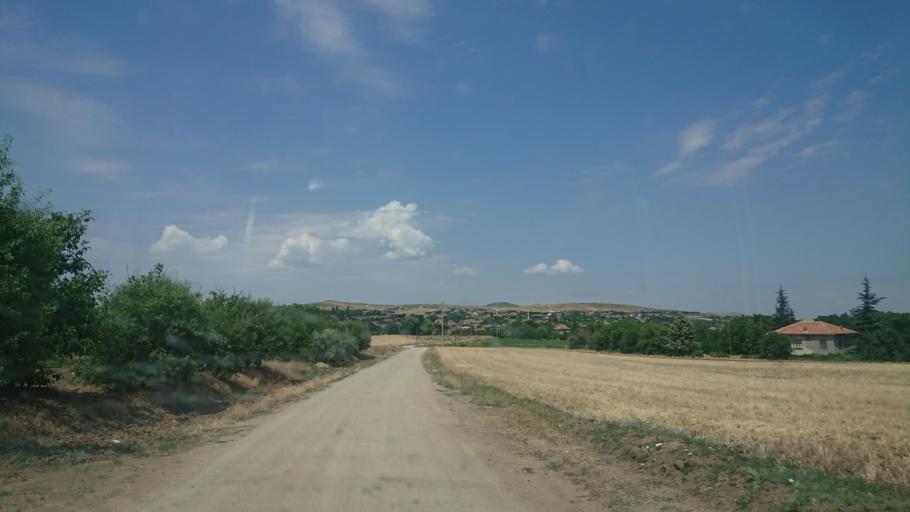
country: TR
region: Aksaray
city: Sariyahsi
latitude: 38.9572
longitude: 33.8988
